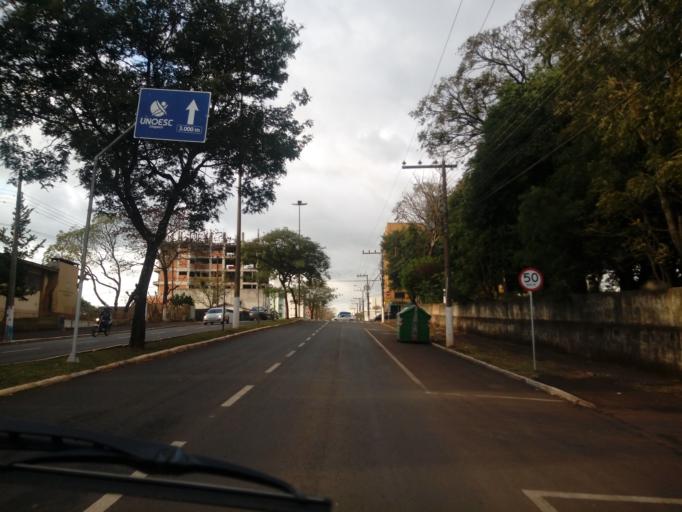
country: BR
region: Santa Catarina
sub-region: Chapeco
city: Chapeco
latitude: -27.1104
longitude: -52.6107
